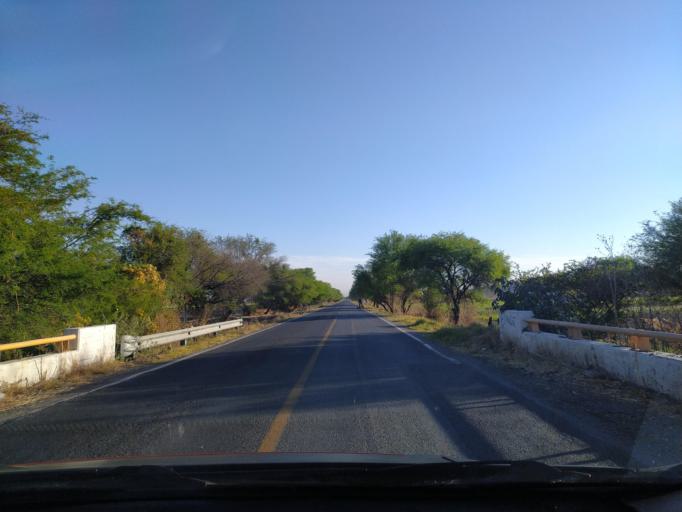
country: MX
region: Guanajuato
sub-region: San Francisco del Rincon
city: San Ignacio de Hidalgo
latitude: 20.9194
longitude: -101.8561
